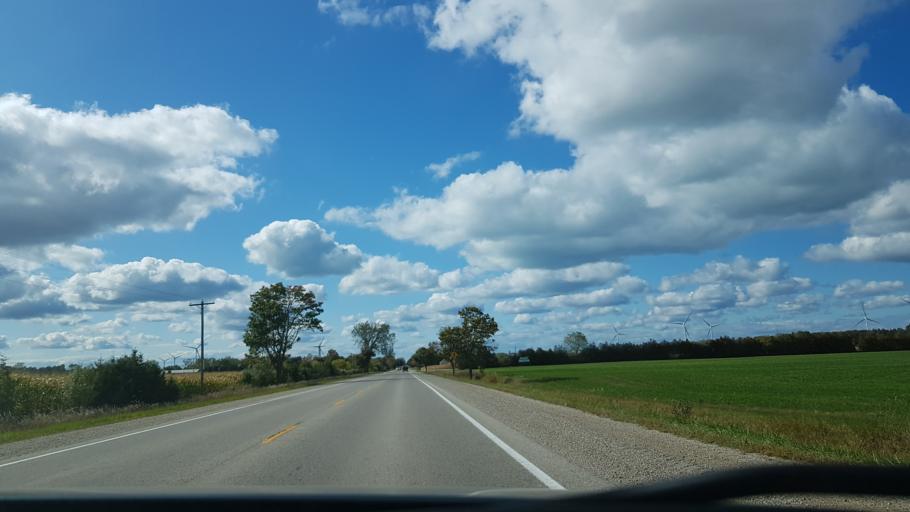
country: CA
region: Ontario
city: Bluewater
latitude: 43.3412
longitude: -81.6815
